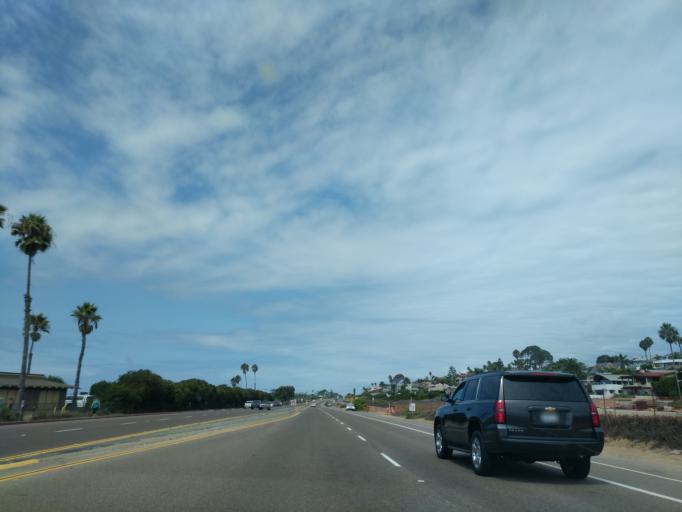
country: US
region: California
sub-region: San Diego County
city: Encinitas
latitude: 33.0248
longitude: -117.2858
